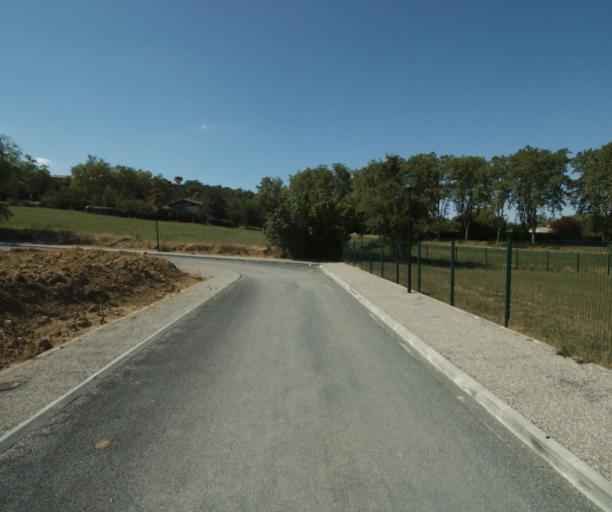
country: FR
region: Midi-Pyrenees
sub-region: Departement de la Haute-Garonne
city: Saint-Felix-Lauragais
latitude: 43.4887
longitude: 1.9031
